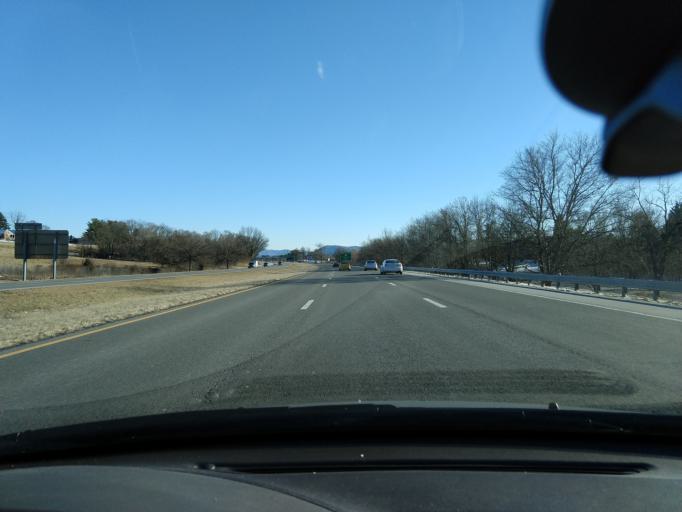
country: US
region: Virginia
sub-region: Roanoke County
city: Hollins
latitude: 37.3184
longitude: -79.9835
